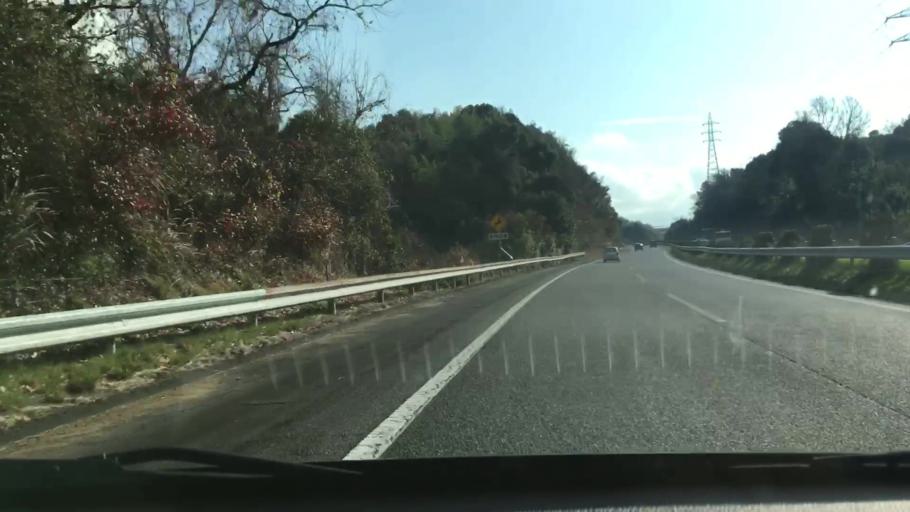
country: JP
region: Kumamoto
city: Matsubase
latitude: 32.6345
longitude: 130.7102
